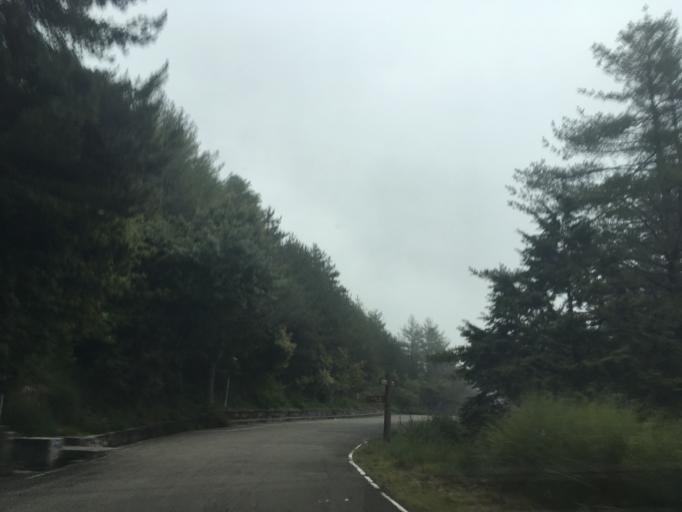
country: TW
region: Taiwan
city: Fengyuan
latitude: 24.2822
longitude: 121.0285
